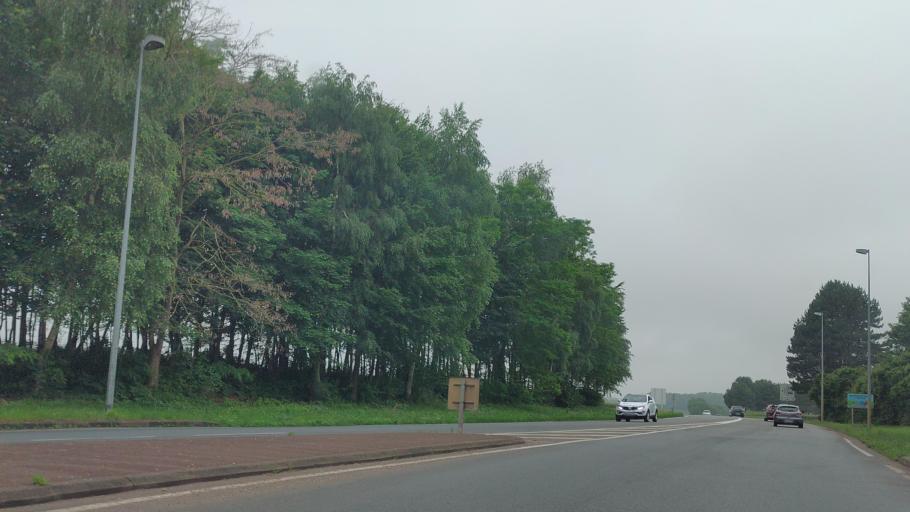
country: FR
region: Picardie
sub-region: Departement de la Somme
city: Friville-Escarbotin
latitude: 50.0732
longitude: 1.5576
